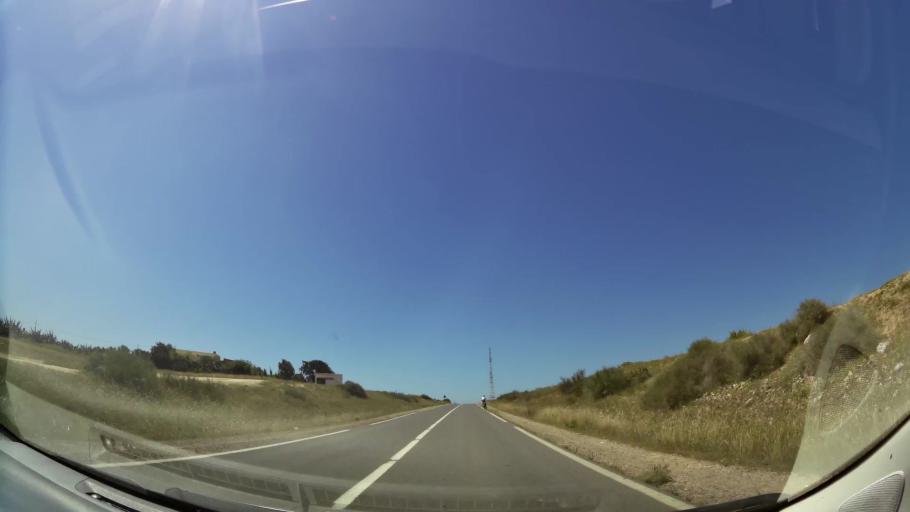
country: MA
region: Oriental
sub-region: Berkane-Taourirt
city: Madagh
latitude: 35.1221
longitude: -2.3818
